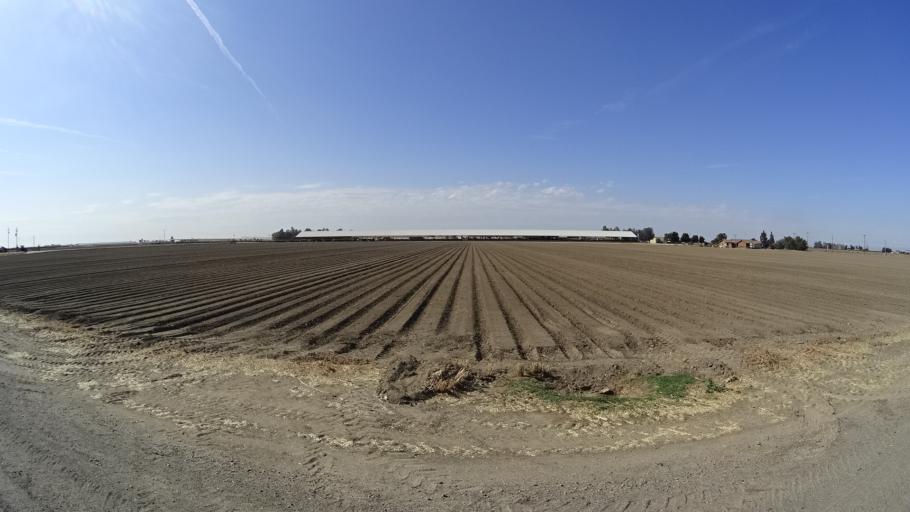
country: US
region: California
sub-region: Kings County
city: Home Garden
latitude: 36.2259
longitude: -119.6256
